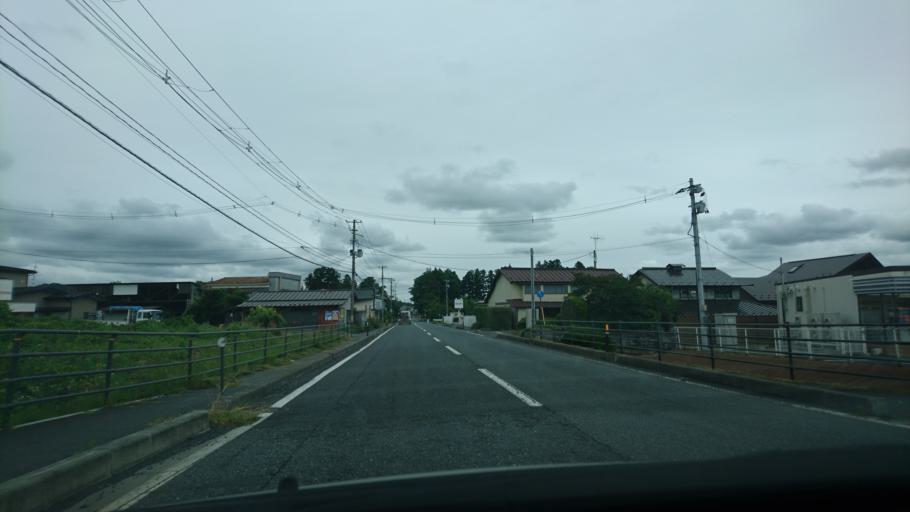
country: JP
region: Iwate
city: Ichinoseki
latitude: 38.9740
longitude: 141.1176
